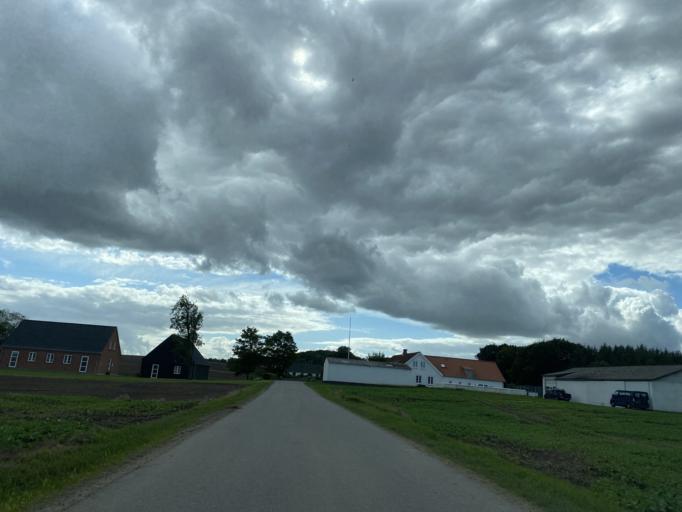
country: DK
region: Central Jutland
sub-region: Horsens Kommune
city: Horsens
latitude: 55.9596
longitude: 9.8585
